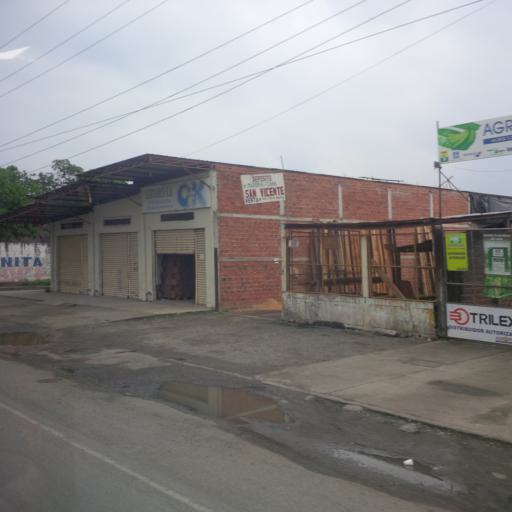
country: EC
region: Canar
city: La Troncal
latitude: -2.3355
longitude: -79.3960
